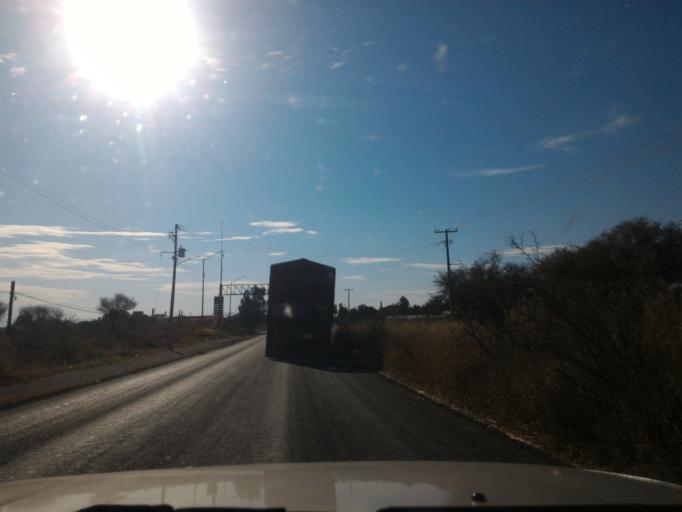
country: MX
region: Guanajuato
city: Ciudad Manuel Doblado
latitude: 20.7398
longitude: -101.9550
